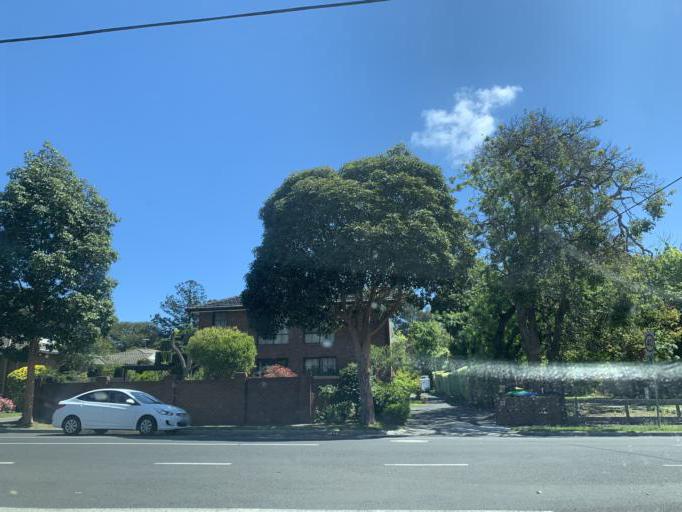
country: AU
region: Victoria
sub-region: Bayside
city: Brighton East
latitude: -37.9057
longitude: 145.0148
